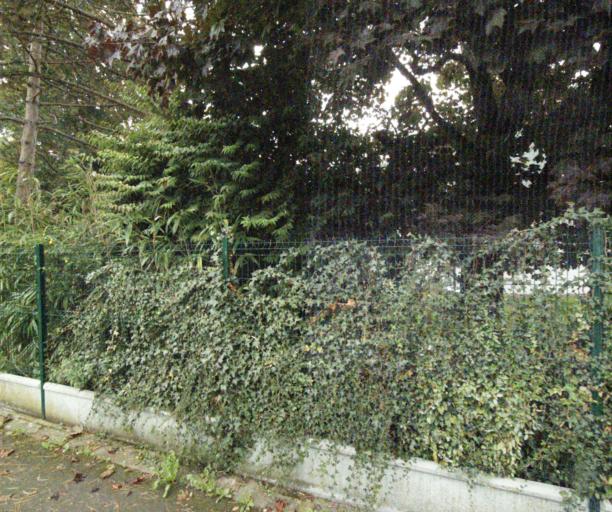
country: FR
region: Nord-Pas-de-Calais
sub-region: Departement du Nord
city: Seclin
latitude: 50.5452
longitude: 3.0226
